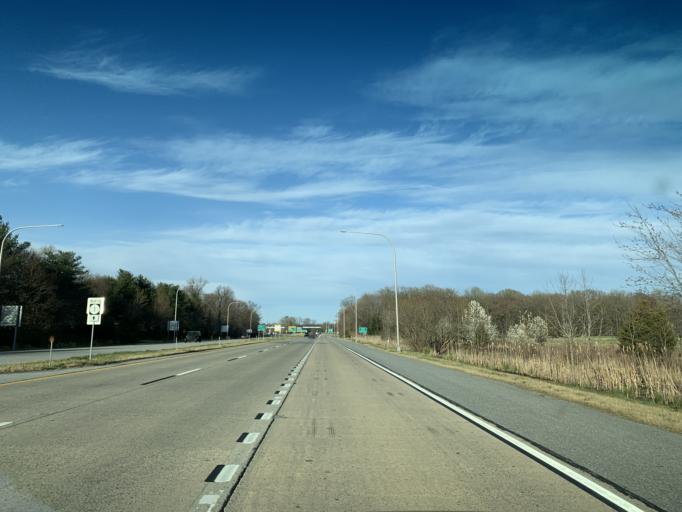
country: US
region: Delaware
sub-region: Kent County
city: Cheswold
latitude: 39.2021
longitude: -75.5525
